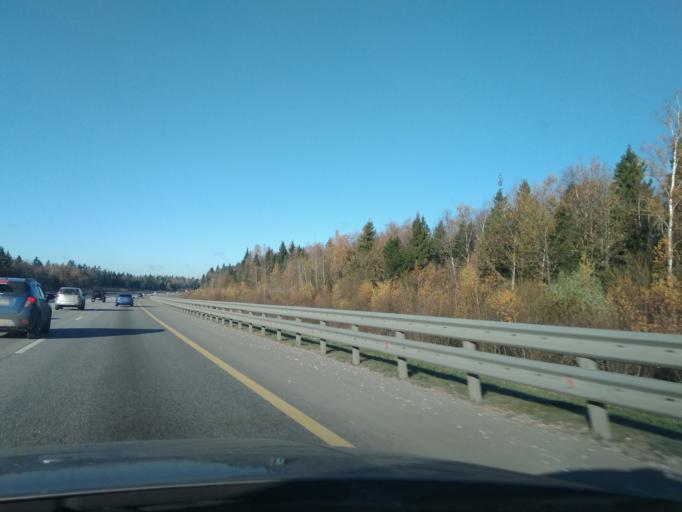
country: RU
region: Moskovskaya
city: Yershovo
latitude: 55.8299
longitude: 36.8656
